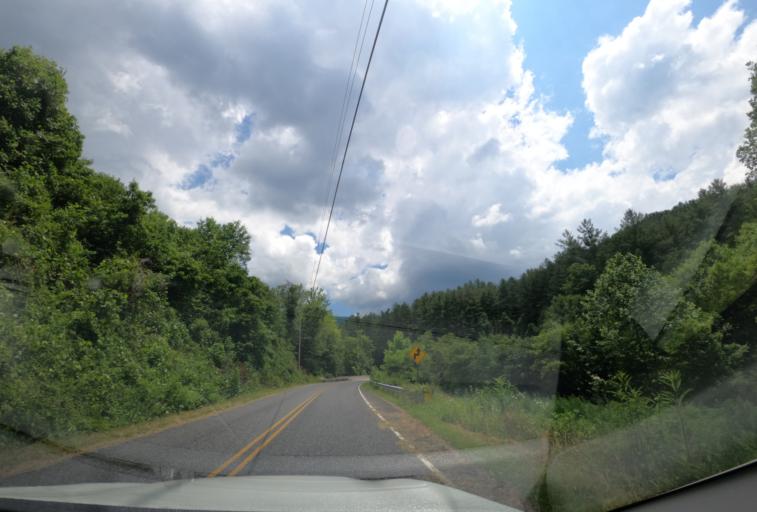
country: US
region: North Carolina
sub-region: Haywood County
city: Hazelwood
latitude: 35.4066
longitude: -82.9032
